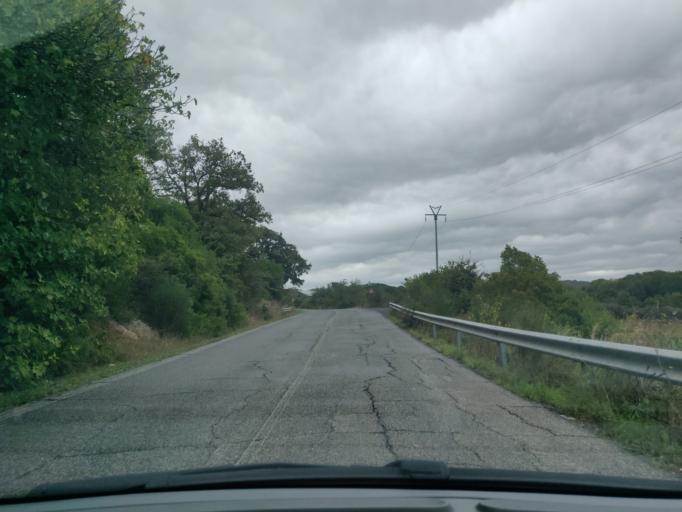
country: IT
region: Latium
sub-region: Citta metropolitana di Roma Capitale
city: Allumiere
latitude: 42.1255
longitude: 11.8613
